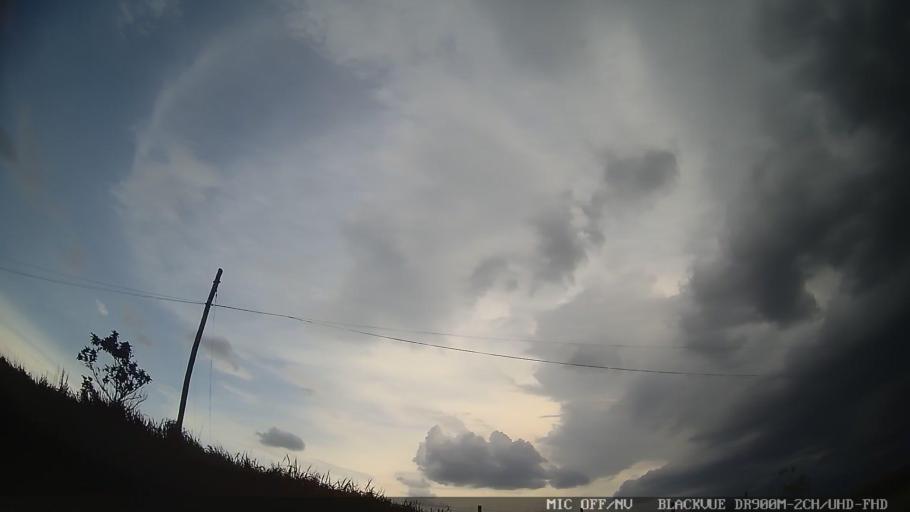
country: BR
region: Sao Paulo
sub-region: Itatiba
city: Itatiba
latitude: -22.9537
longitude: -46.8198
